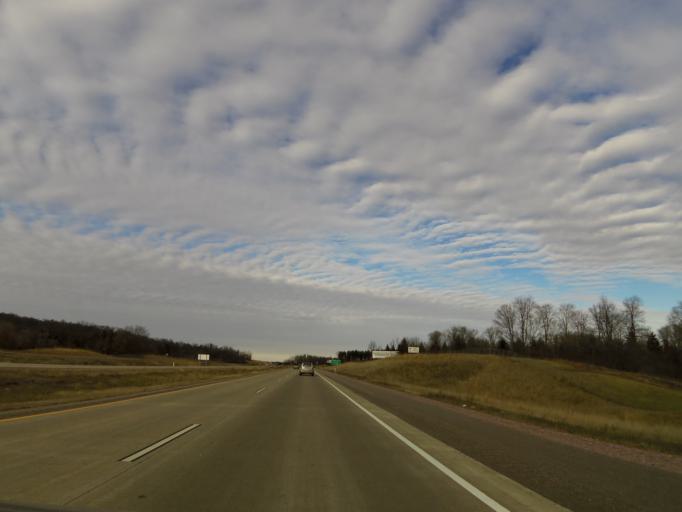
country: US
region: Wisconsin
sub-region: Sauk County
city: West Baraboo
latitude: 43.4996
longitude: -89.7815
